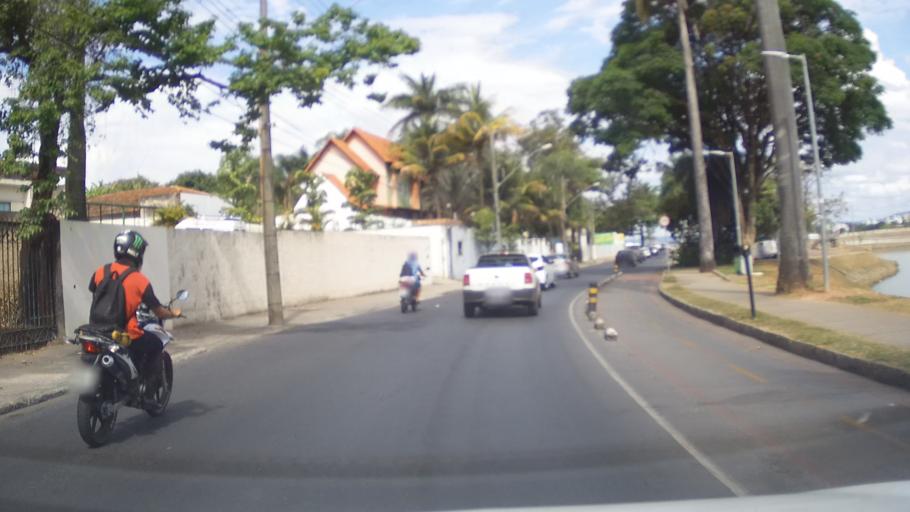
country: BR
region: Minas Gerais
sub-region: Belo Horizonte
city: Belo Horizonte
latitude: -19.8436
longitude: -43.9690
